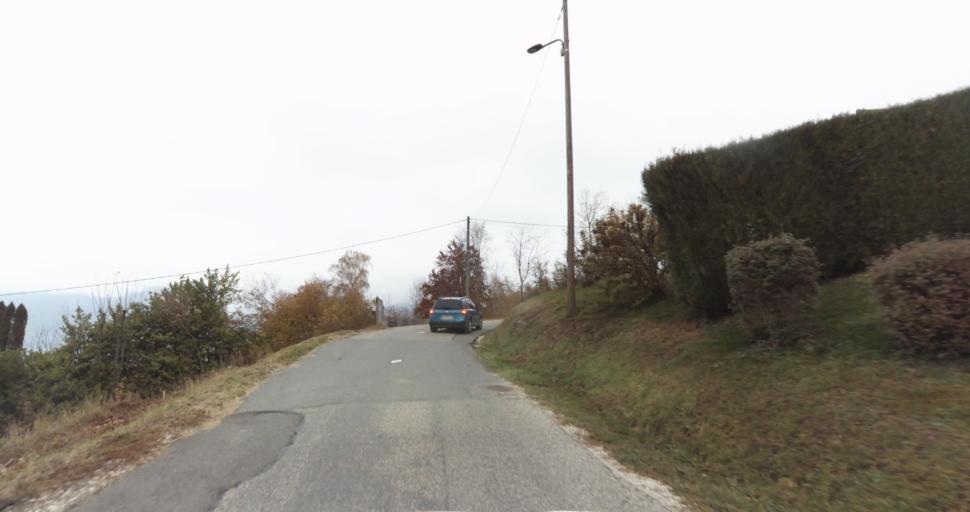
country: FR
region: Rhone-Alpes
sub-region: Departement de la Haute-Savoie
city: Saint-Jorioz
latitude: 45.8194
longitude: 6.1718
